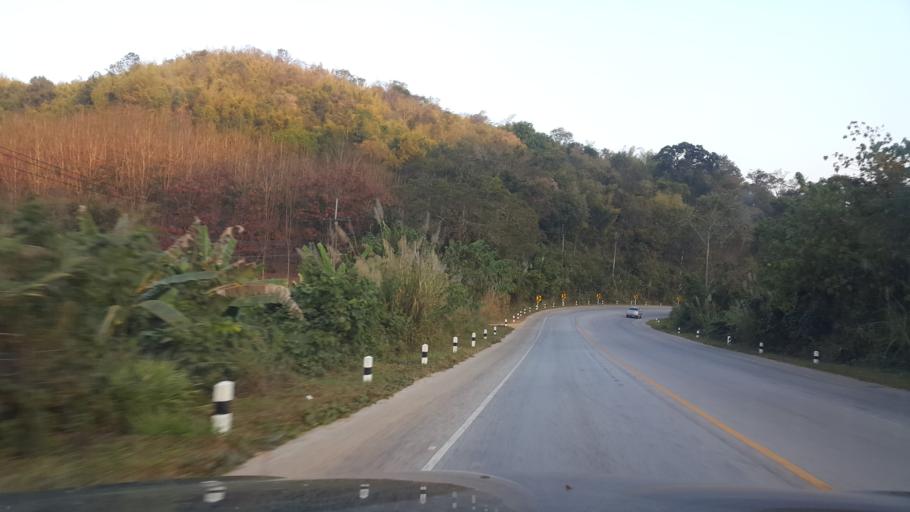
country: TH
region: Loei
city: Loei
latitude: 17.4782
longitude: 101.5596
